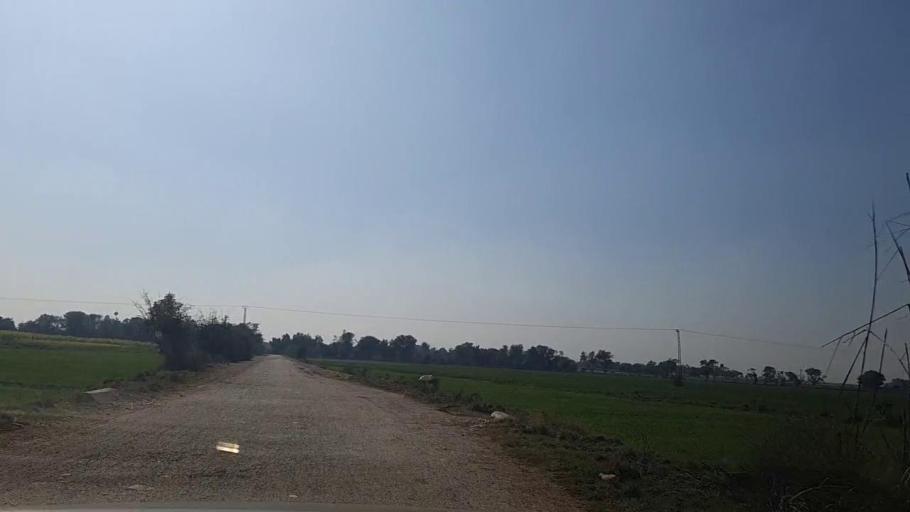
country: PK
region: Sindh
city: Sehwan
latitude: 26.2810
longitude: 68.0406
